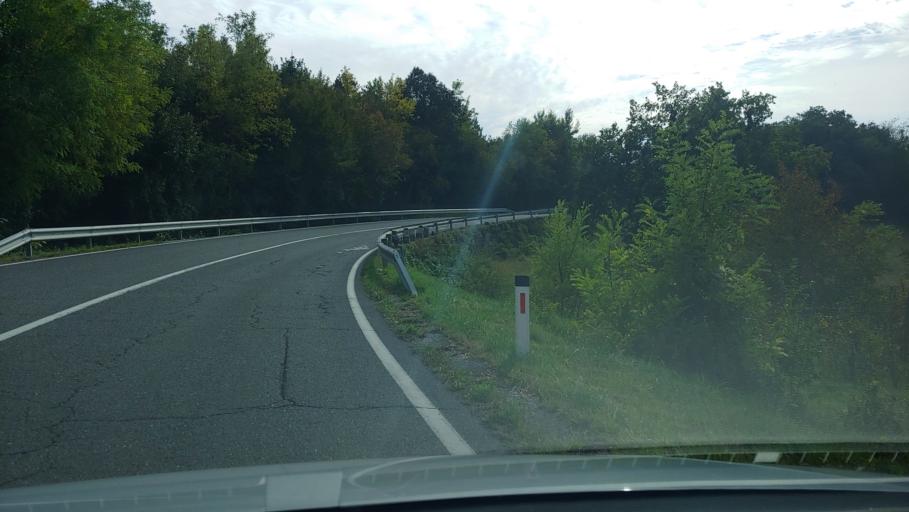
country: SI
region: Nova Gorica
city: Sempas
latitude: 45.9129
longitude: 13.7680
